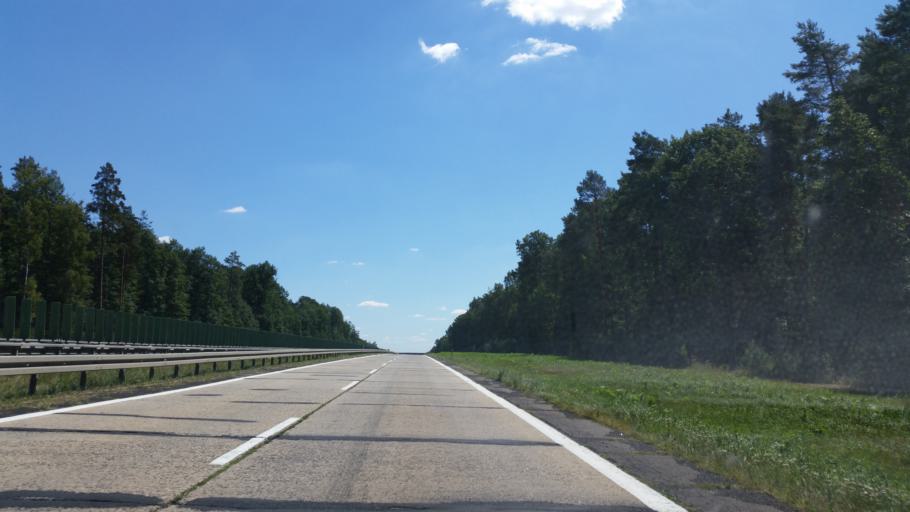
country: PL
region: Lower Silesian Voivodeship
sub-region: Powiat boleslawiecki
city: Boleslawiec
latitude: 51.3958
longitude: 15.5273
